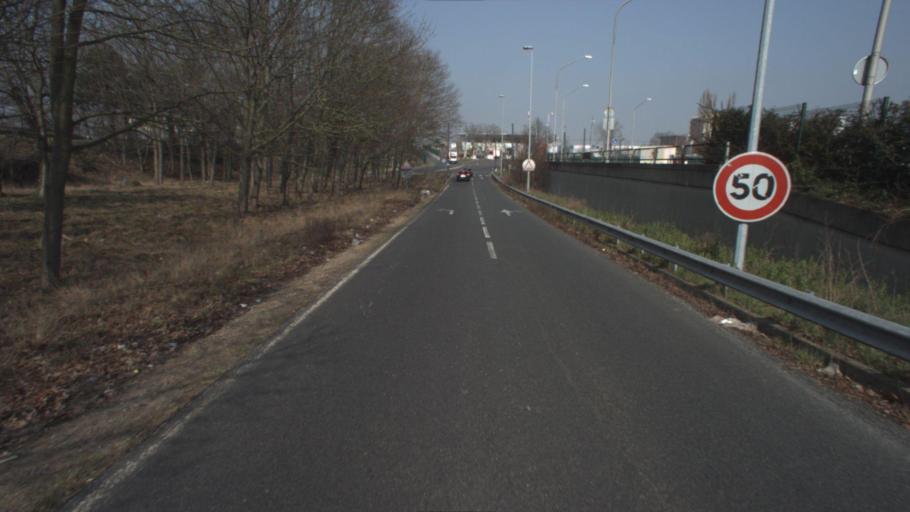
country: FR
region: Ile-de-France
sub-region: Departement du Val-de-Marne
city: Rungis
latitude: 48.7514
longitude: 2.3554
